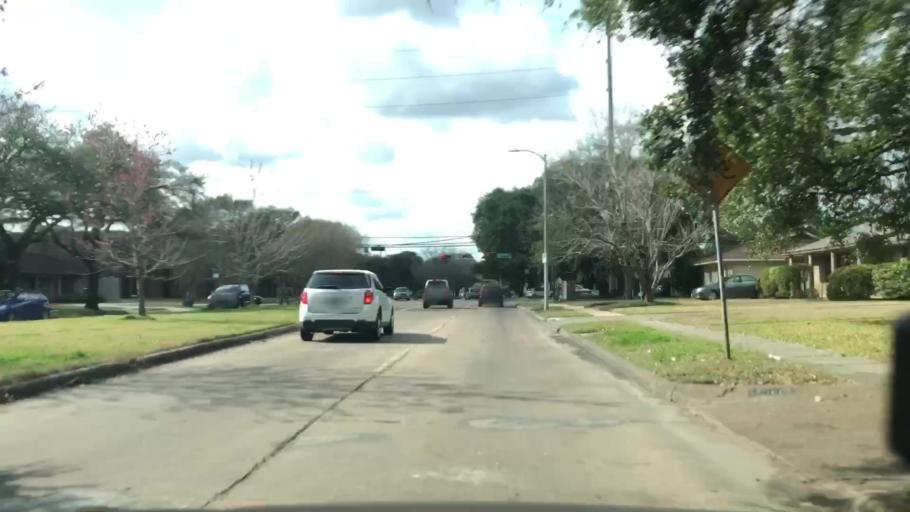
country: US
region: Texas
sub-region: Harris County
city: Bellaire
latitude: 29.6892
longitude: -95.4835
